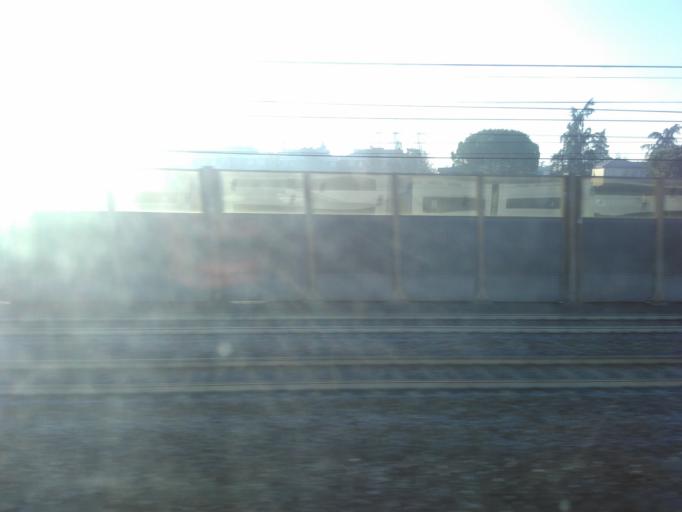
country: IT
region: Veneto
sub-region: Provincia di Padova
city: Noventa
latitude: 45.4274
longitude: 11.9387
